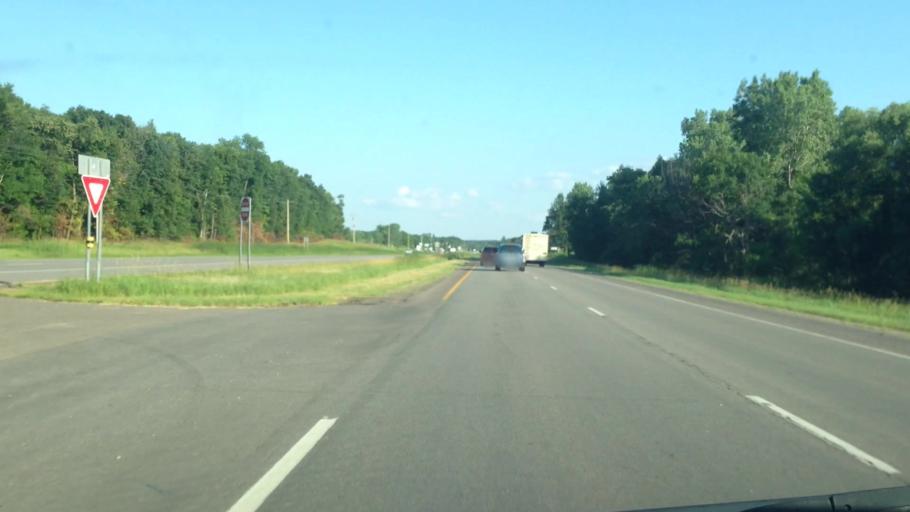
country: US
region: Minnesota
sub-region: Sherburne County
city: Zimmerman
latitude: 45.4363
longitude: -93.5806
